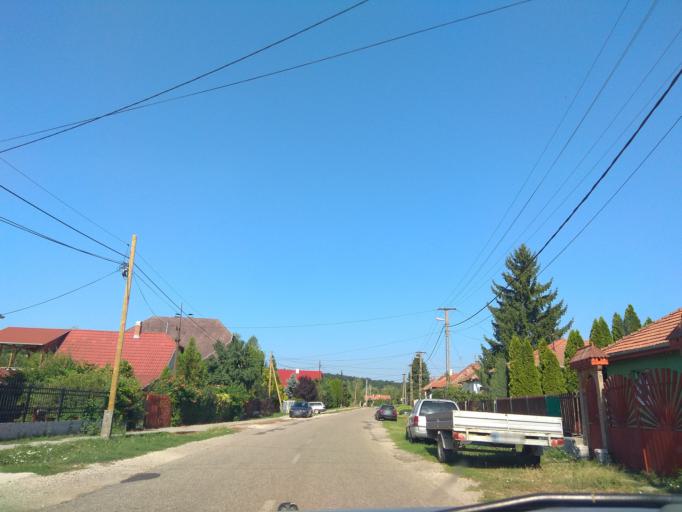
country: HU
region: Borsod-Abauj-Zemplen
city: Harsany
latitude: 47.9908
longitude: 20.7714
